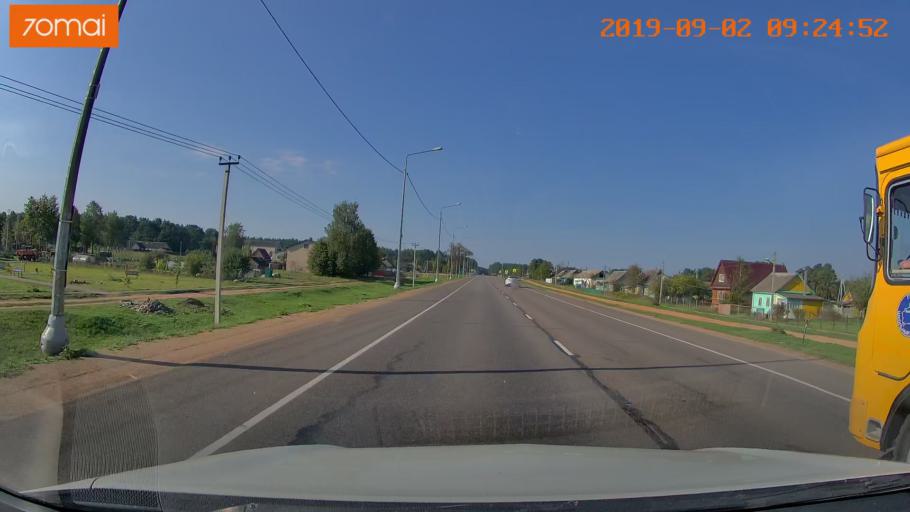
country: RU
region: Kaluga
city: Yukhnov
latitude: 54.7624
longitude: 35.2863
